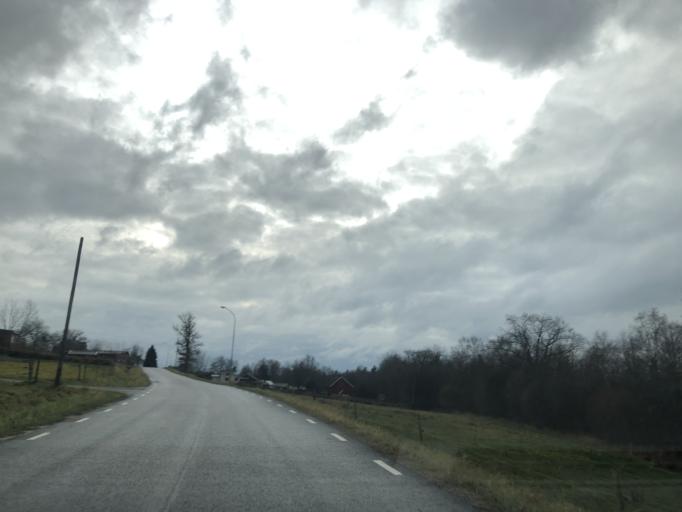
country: SE
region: Vaestra Goetaland
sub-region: Ulricehamns Kommun
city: Ulricehamn
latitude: 57.8187
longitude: 13.2450
